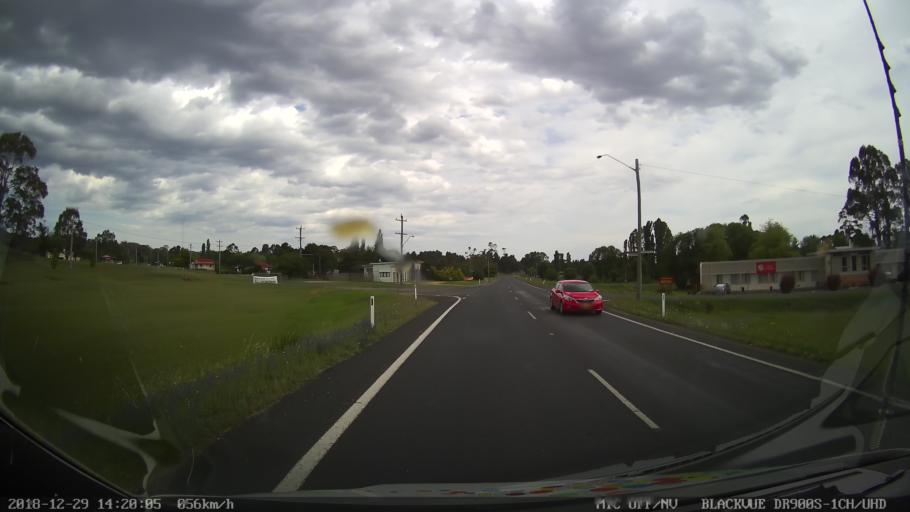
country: AU
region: New South Wales
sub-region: Cooma-Monaro
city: Cooma
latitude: -36.5052
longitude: 149.2851
